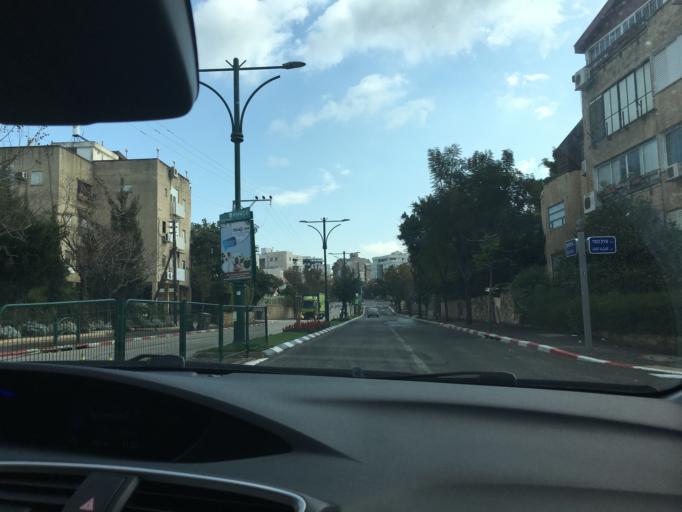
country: IL
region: Tel Aviv
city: Ramat HaSharon
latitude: 32.1606
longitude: 34.8433
